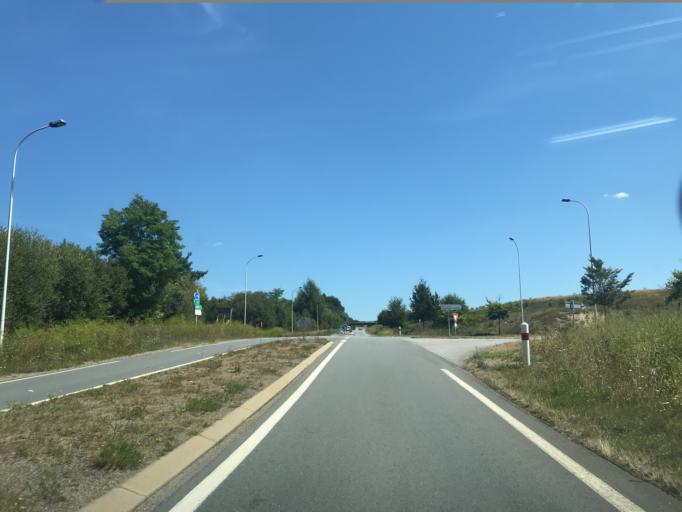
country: FR
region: Limousin
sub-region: Departement de la Correze
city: Correze
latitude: 45.3337
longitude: 1.8901
